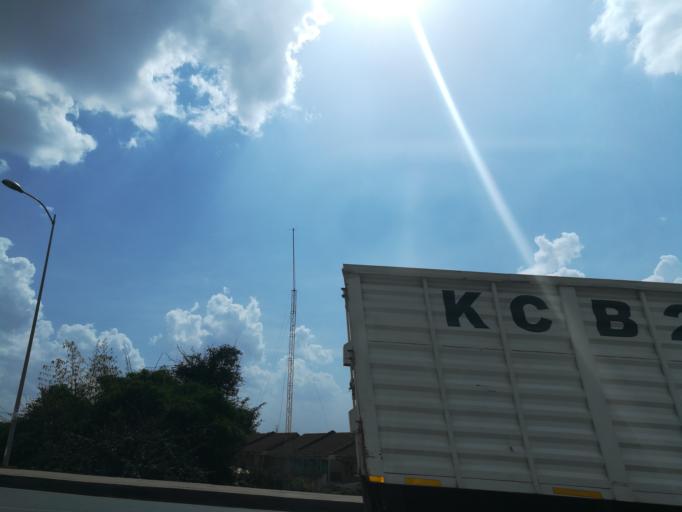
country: KE
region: Nairobi Area
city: Pumwani
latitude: -1.3229
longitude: 36.8482
